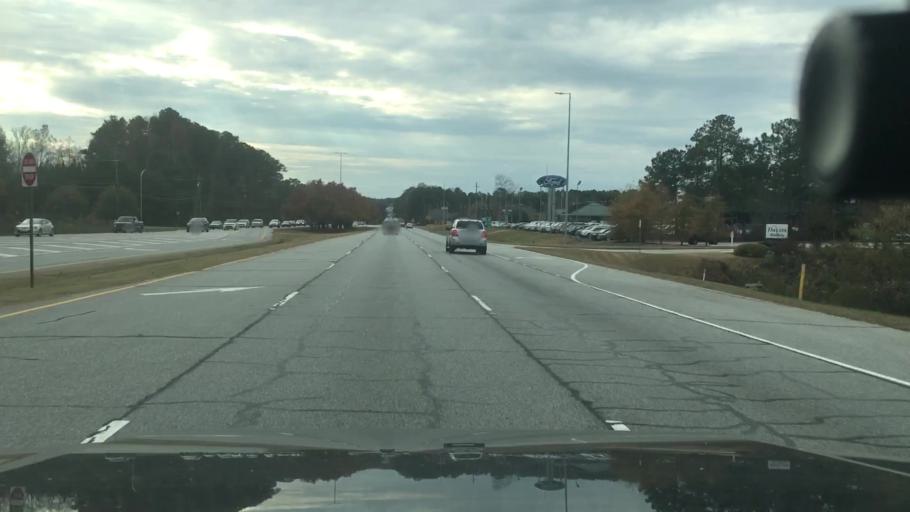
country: US
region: Georgia
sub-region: Coweta County
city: Newnan
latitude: 33.3928
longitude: -84.7672
